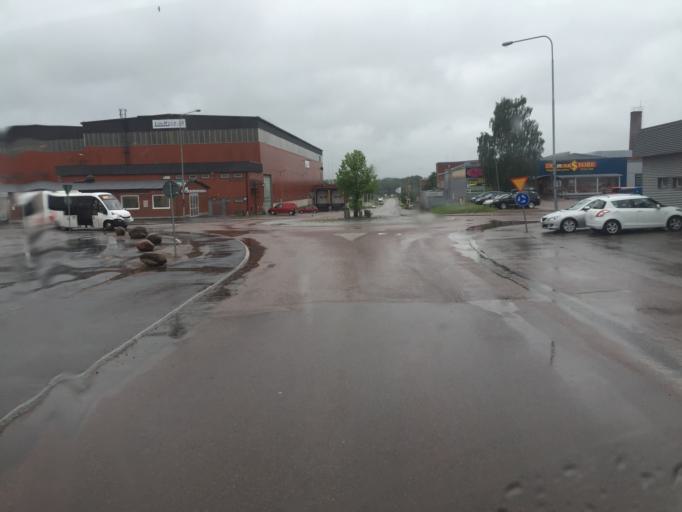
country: SE
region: Dalarna
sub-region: Borlange Kommun
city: Borlaenge
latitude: 60.4764
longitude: 15.4354
